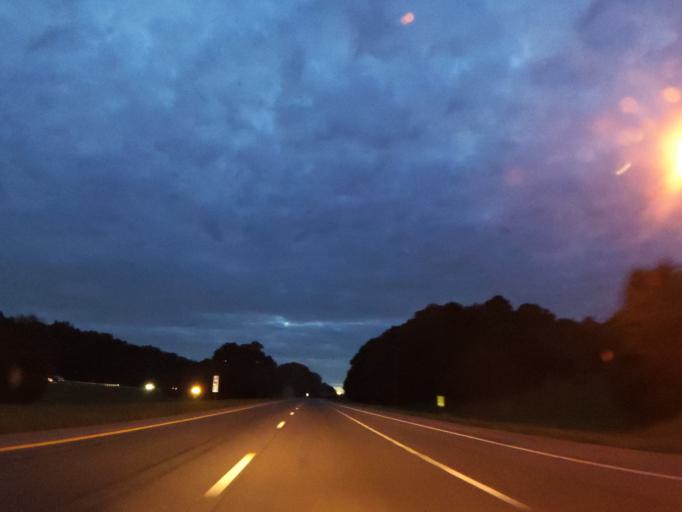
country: US
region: Tennessee
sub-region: Cheatham County
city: Pleasant View
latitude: 36.4061
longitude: -87.0318
